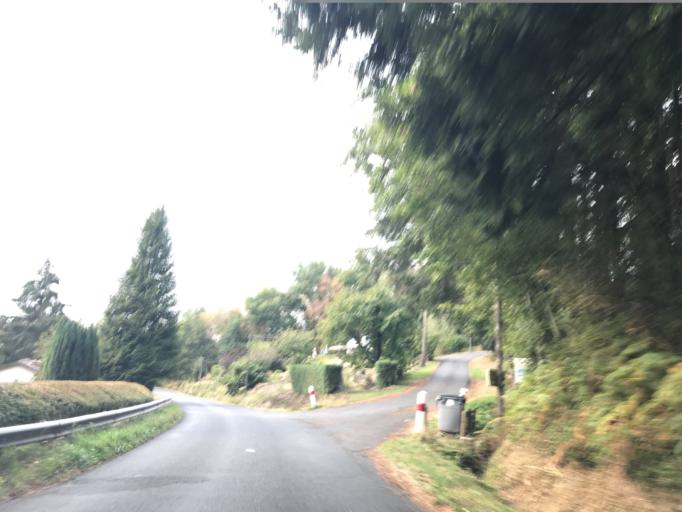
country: FR
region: Auvergne
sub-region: Departement du Puy-de-Dome
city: Escoutoux
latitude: 45.7956
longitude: 3.6147
